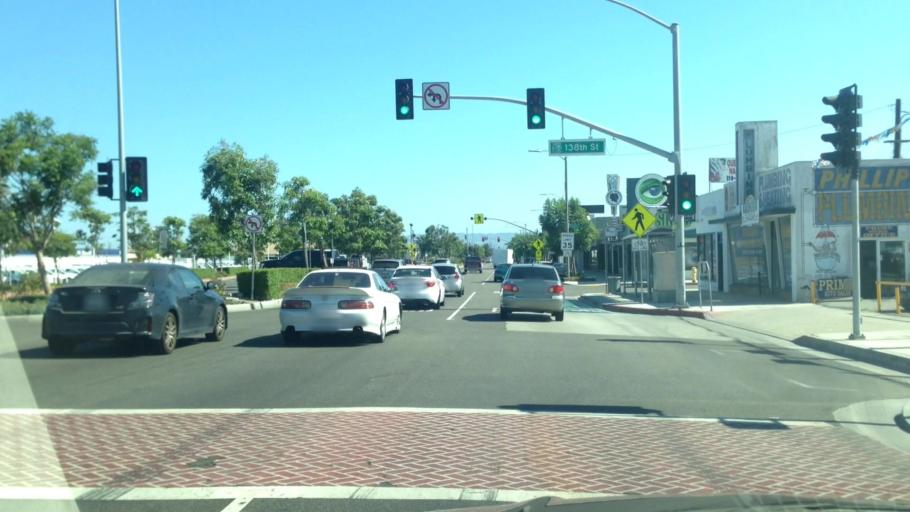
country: US
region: California
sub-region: Los Angeles County
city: Hawthorne
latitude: 33.9065
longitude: -118.3528
